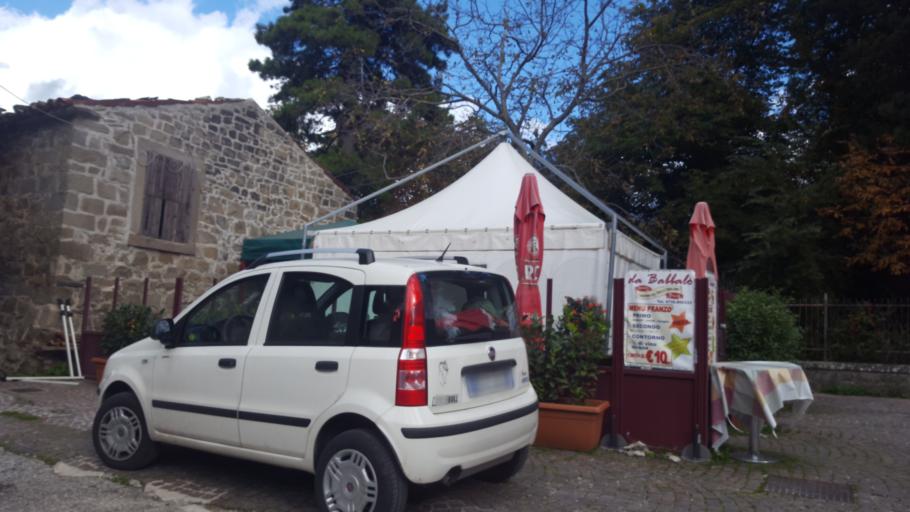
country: IT
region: The Marches
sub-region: Provincia di Ascoli Piceno
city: Balzo
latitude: 42.8413
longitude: 13.3327
